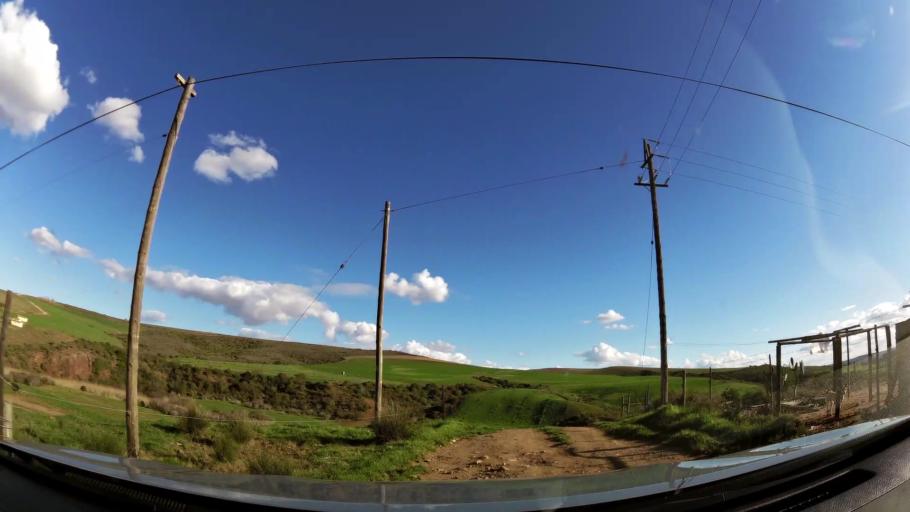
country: ZA
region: Western Cape
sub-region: Eden District Municipality
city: Riversdale
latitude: -34.1114
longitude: 20.9636
